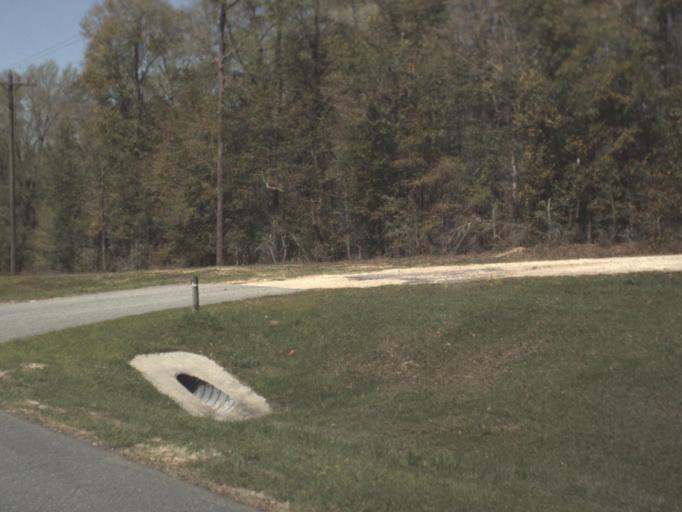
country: US
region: Alabama
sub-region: Geneva County
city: Hartford
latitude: 30.9599
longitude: -85.6644
